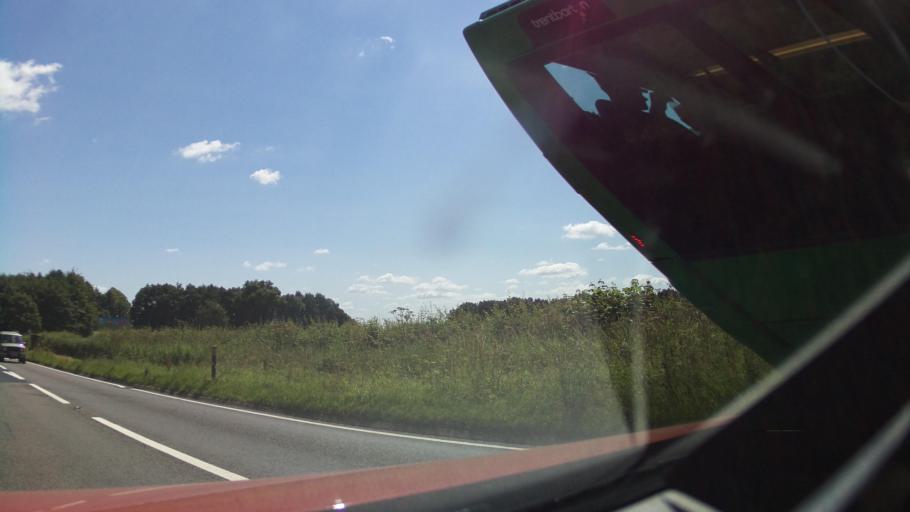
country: GB
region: England
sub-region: Derbyshire
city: Yeldersley
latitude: 52.9758
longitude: -1.6495
